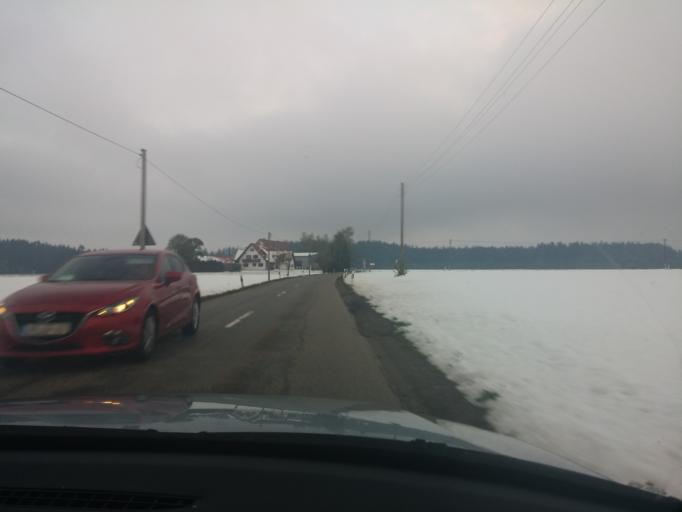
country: DE
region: Bavaria
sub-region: Swabia
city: Kronburg
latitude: 47.9349
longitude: 10.1544
